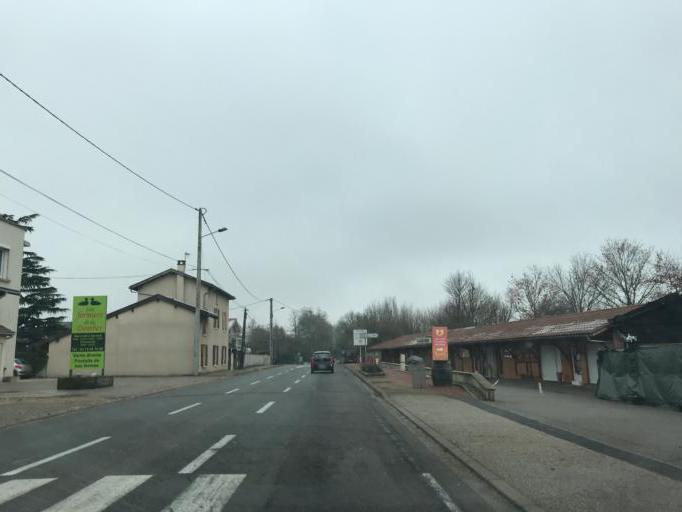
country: FR
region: Rhone-Alpes
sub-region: Departement de l'Ain
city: Villars-les-Dombes
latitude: 45.9966
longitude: 5.0279
